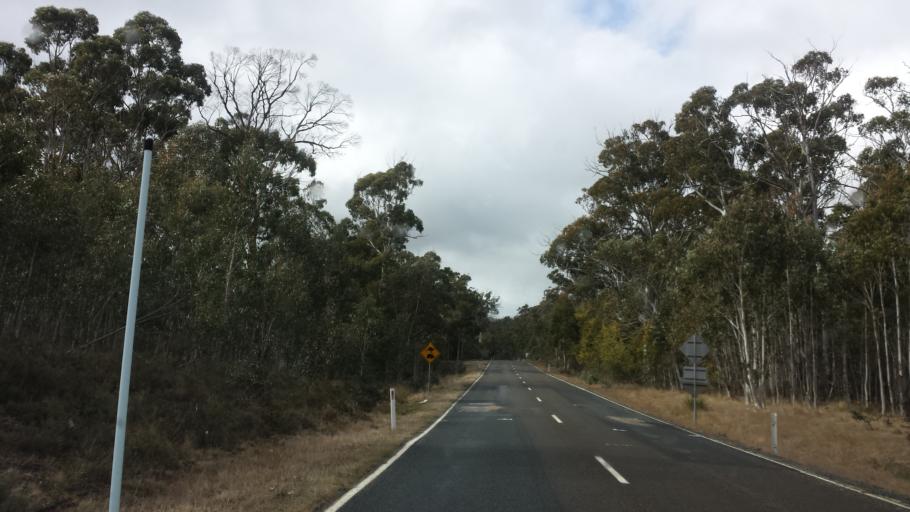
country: AU
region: Victoria
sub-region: Alpine
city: Mount Beauty
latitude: -37.1316
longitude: 147.5187
